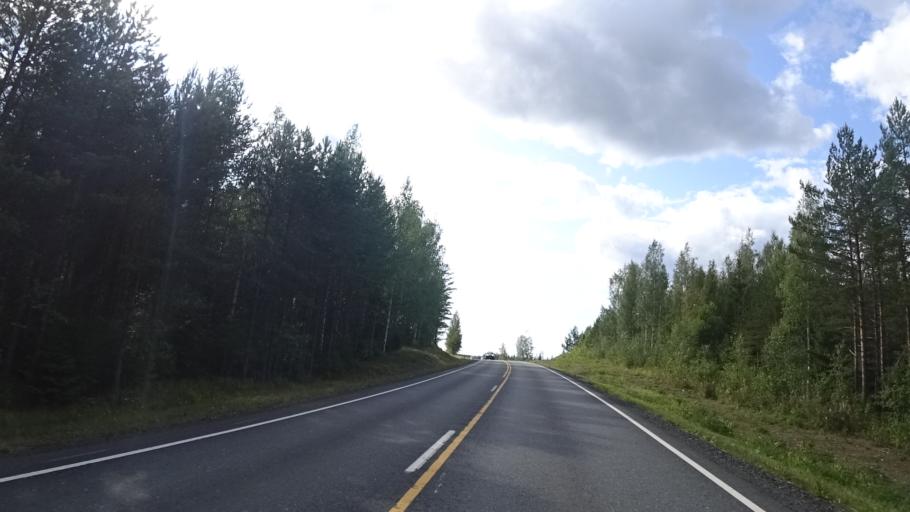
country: FI
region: North Karelia
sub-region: Keski-Karjala
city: Tohmajaervi
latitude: 62.1853
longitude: 30.4975
